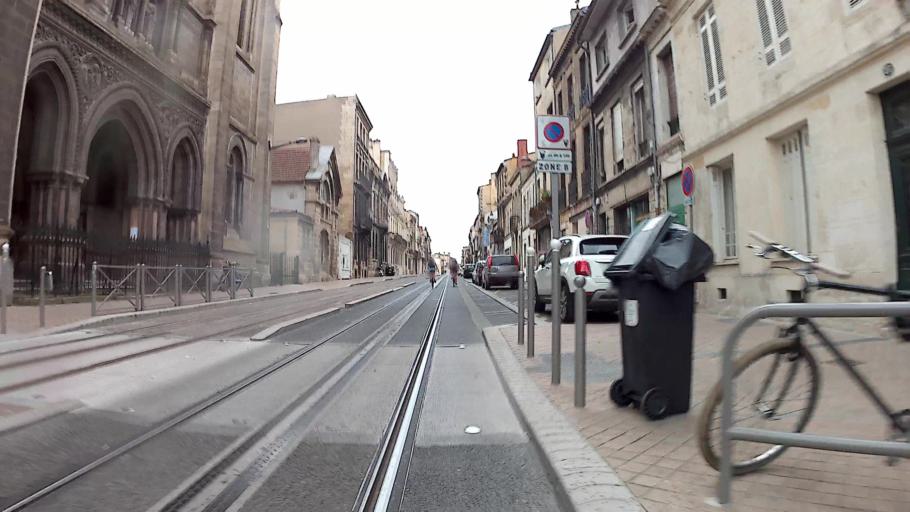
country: FR
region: Aquitaine
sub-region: Departement de la Gironde
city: Bordeaux
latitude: 44.8505
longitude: -0.5871
